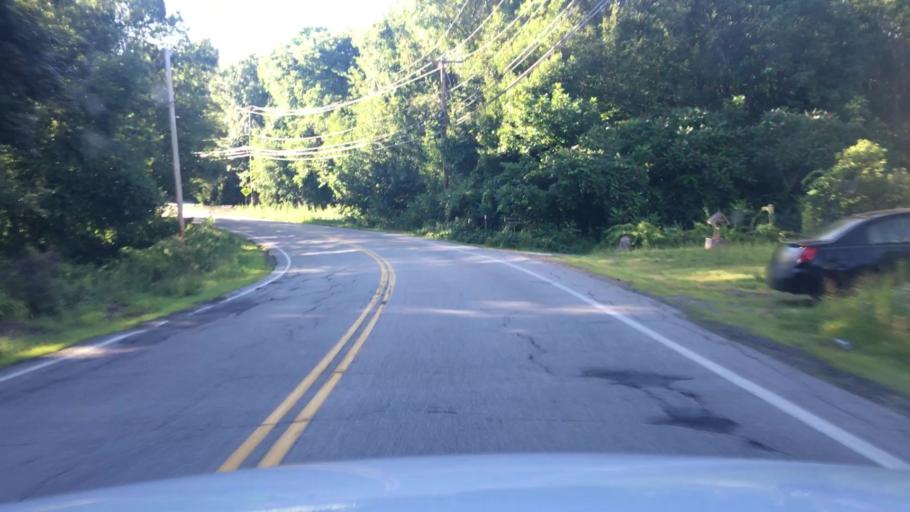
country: US
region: New Hampshire
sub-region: Rockingham County
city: Sandown
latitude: 42.9158
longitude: -71.1649
